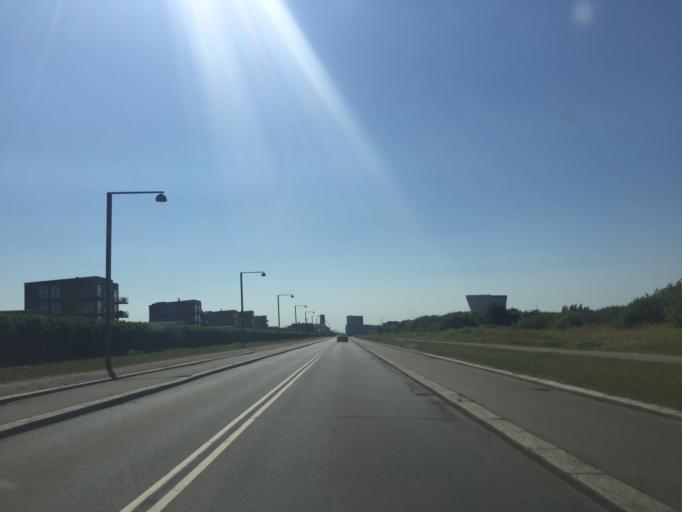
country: DK
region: Capital Region
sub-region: Tarnby Kommune
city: Tarnby
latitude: 55.6494
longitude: 12.5869
